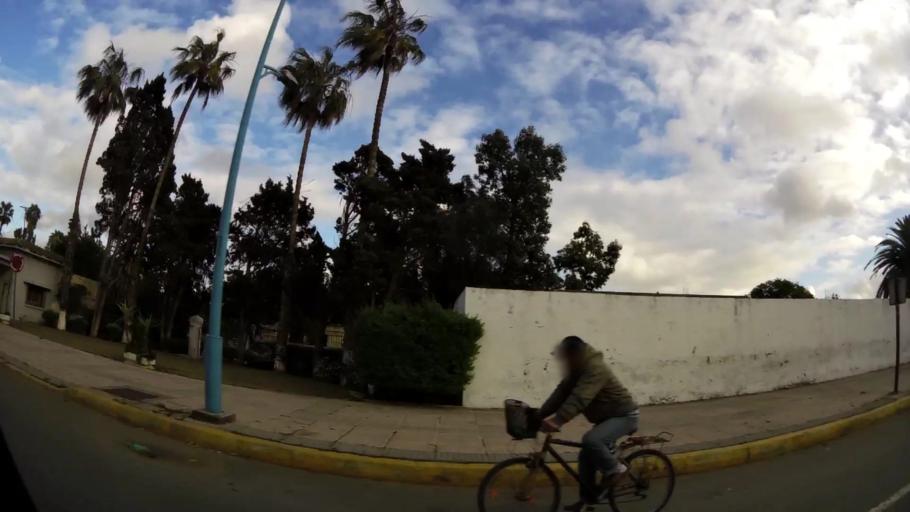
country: MA
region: Grand Casablanca
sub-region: Mohammedia
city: Mohammedia
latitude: 33.7019
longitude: -7.3758
